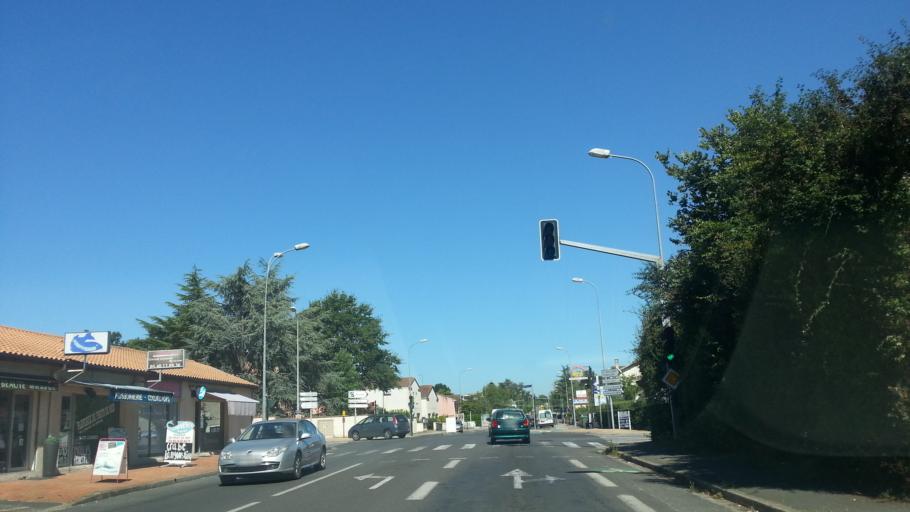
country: FR
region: Aquitaine
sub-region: Departement de la Gironde
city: Villenave-d'Ornon
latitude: 44.7619
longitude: -0.5585
